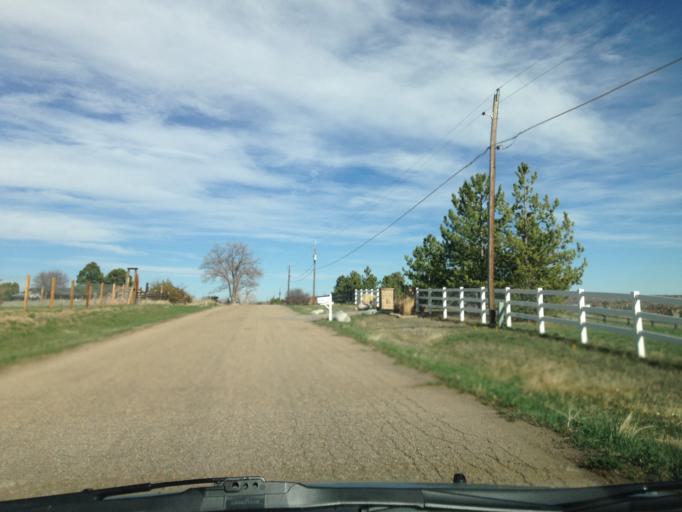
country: US
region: Colorado
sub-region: Boulder County
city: Gunbarrel
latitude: 40.0619
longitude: -105.1272
